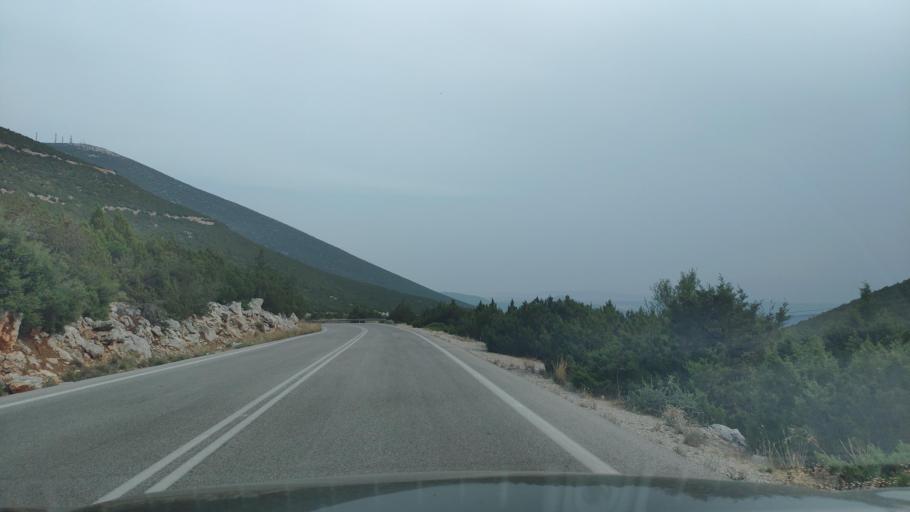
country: GR
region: Peloponnese
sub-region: Nomos Argolidos
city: Didyma
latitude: 37.4992
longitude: 23.1908
